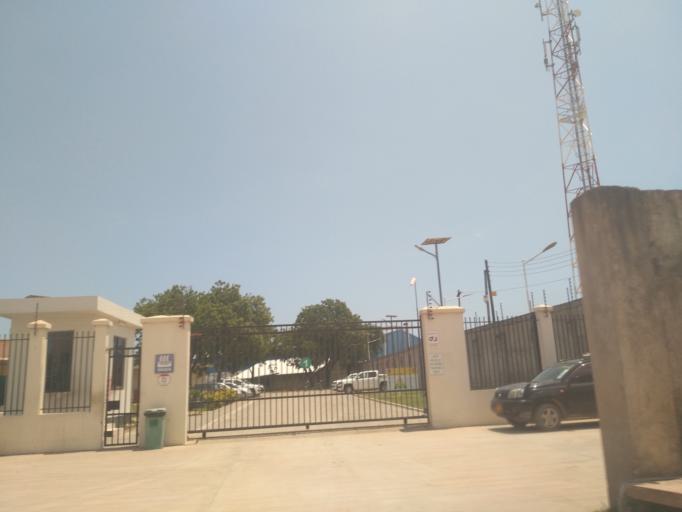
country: TZ
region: Dar es Salaam
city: Dar es Salaam
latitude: -6.8395
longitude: 39.2892
